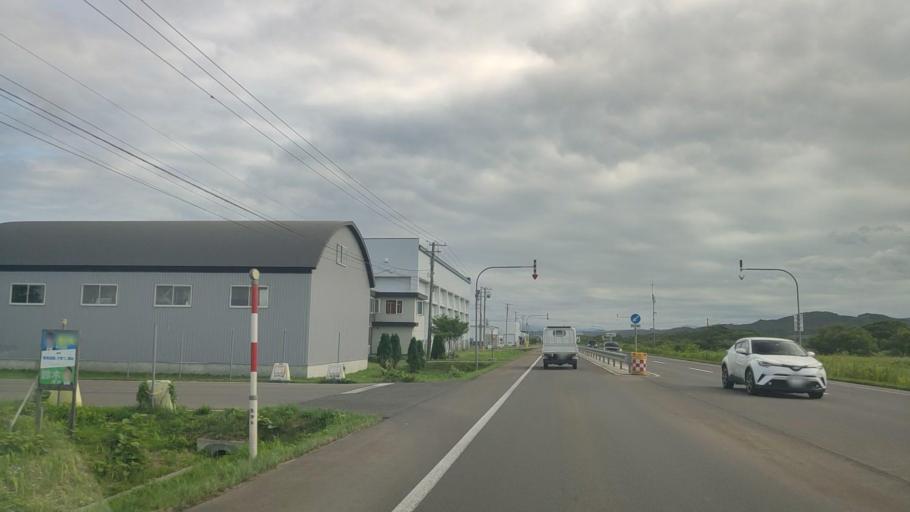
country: JP
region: Hokkaido
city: Niseko Town
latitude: 42.4463
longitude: 140.3290
